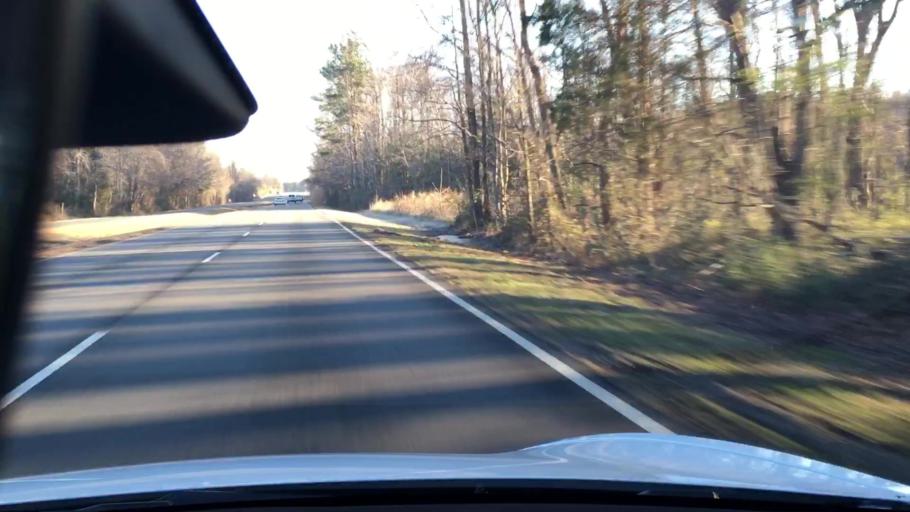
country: US
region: Virginia
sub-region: Henrico County
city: Fort Lee
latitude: 37.4741
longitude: -77.3690
